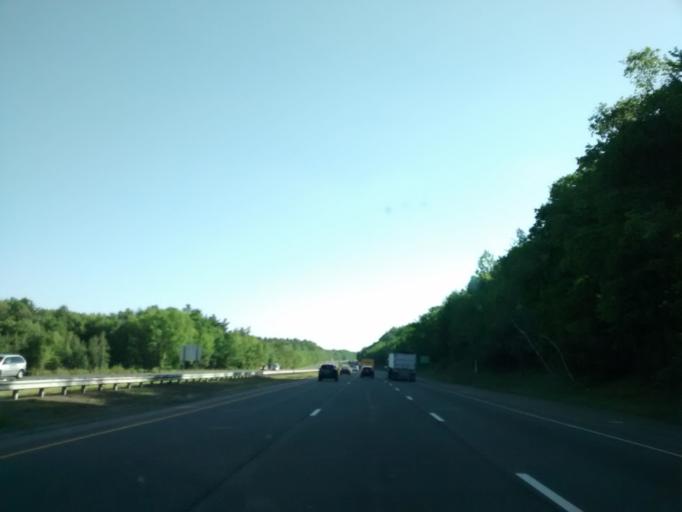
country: US
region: Massachusetts
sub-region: Hampden County
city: Holland
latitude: 42.0074
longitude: -72.1613
